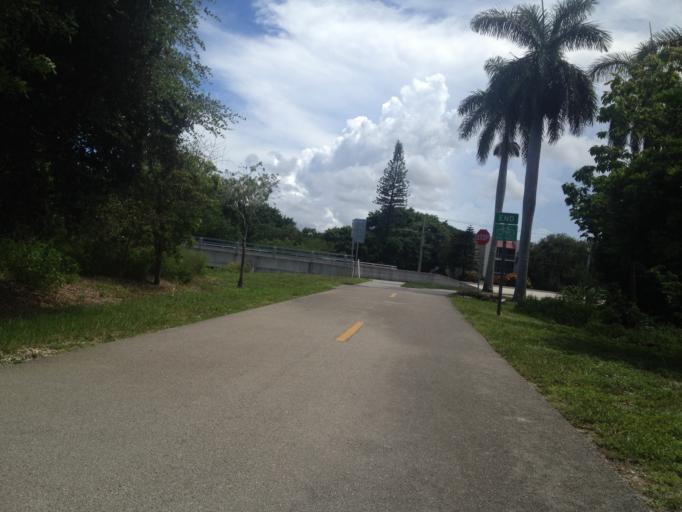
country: US
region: Florida
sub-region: Palm Beach County
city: Boca Raton
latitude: 26.3629
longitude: -80.0970
